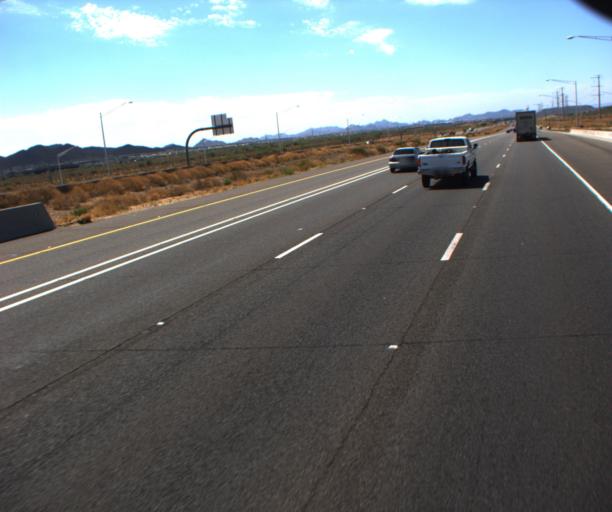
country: US
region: Arizona
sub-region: Maricopa County
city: Anthem
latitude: 33.7687
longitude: -112.1295
